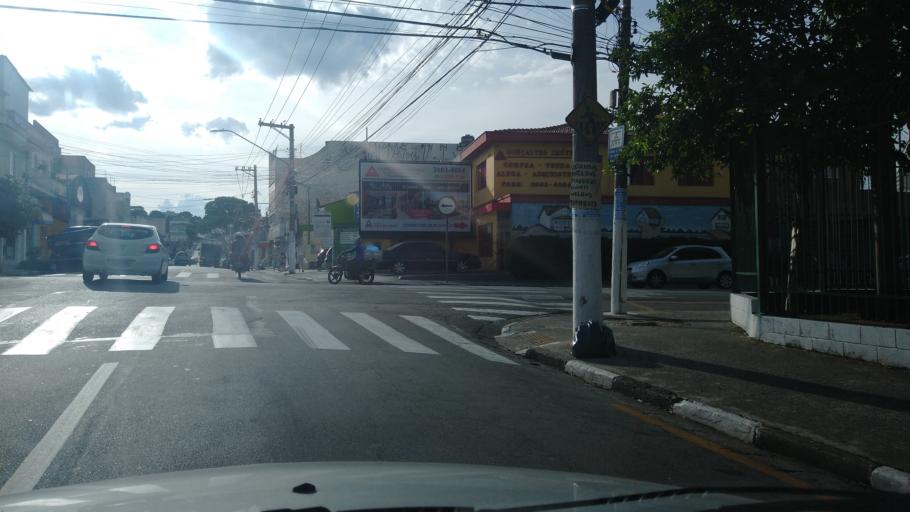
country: BR
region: Sao Paulo
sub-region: Osasco
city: Osasco
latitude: -23.5313
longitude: -46.7973
